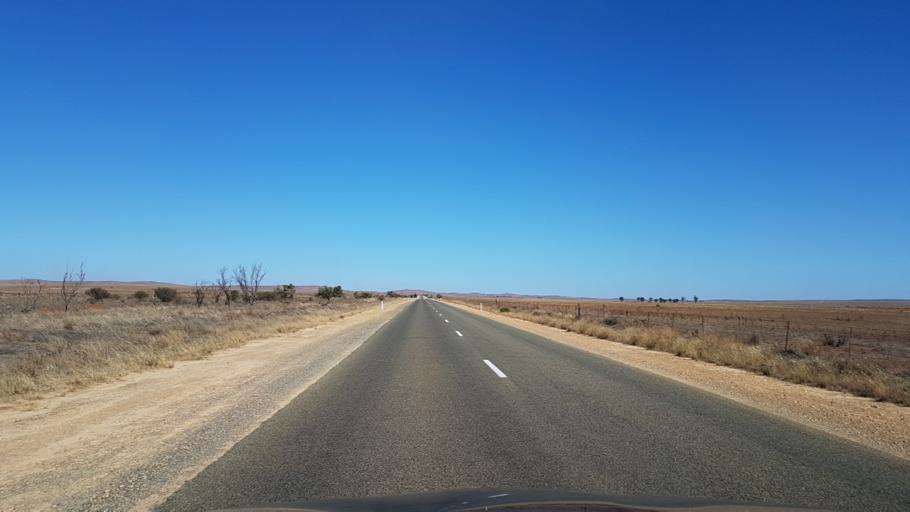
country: AU
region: South Australia
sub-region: Peterborough
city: Peterborough
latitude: -32.9985
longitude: 138.8503
